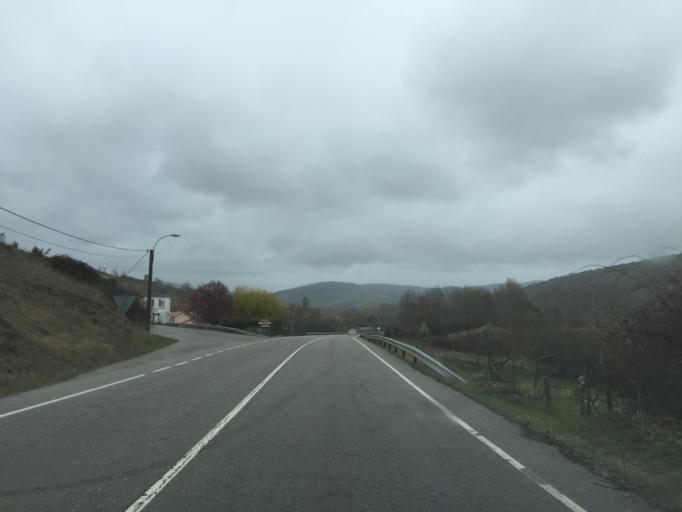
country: ES
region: Castille and Leon
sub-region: Provincia de Leon
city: Carrocera
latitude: 42.7857
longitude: -5.7750
